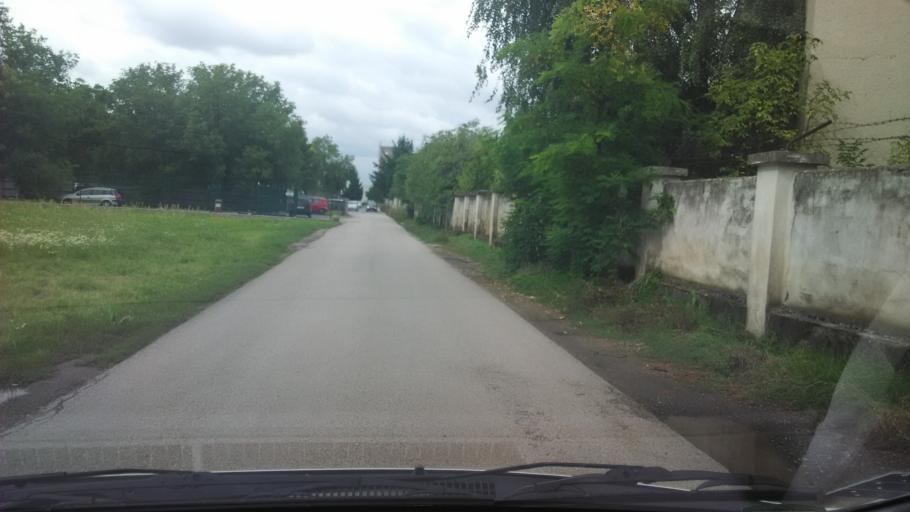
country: SK
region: Nitriansky
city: Levice
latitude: 48.2106
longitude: 18.5835
